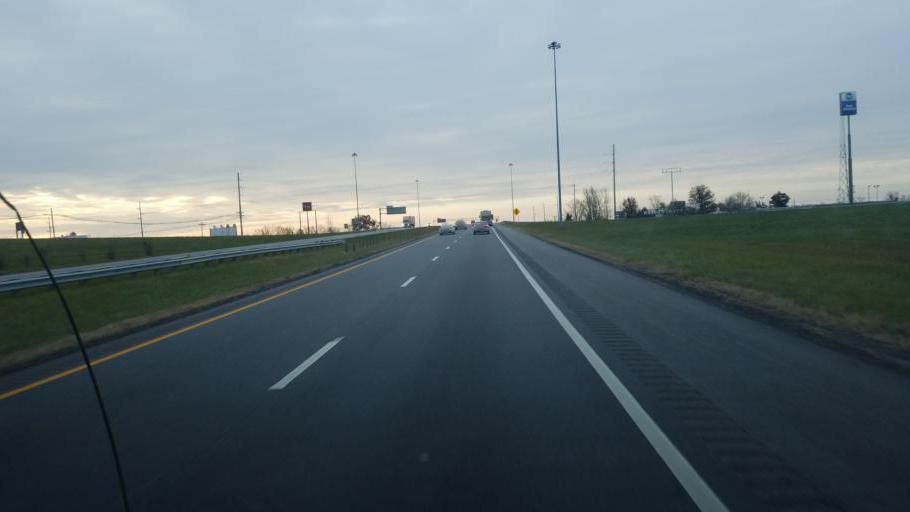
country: US
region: Ohio
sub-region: Auglaize County
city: Wapakoneta
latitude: 40.5610
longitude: -84.1701
